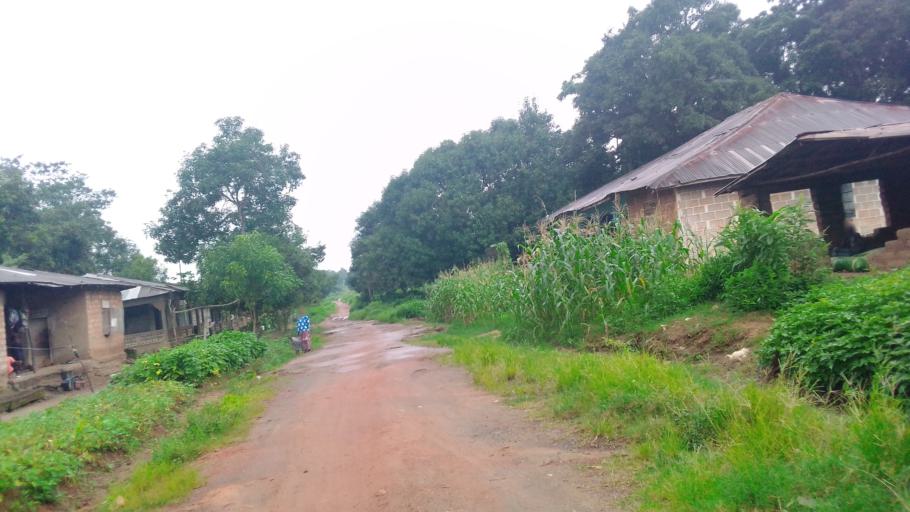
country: SL
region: Northern Province
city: Lunsar
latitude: 8.6887
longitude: -12.5222
